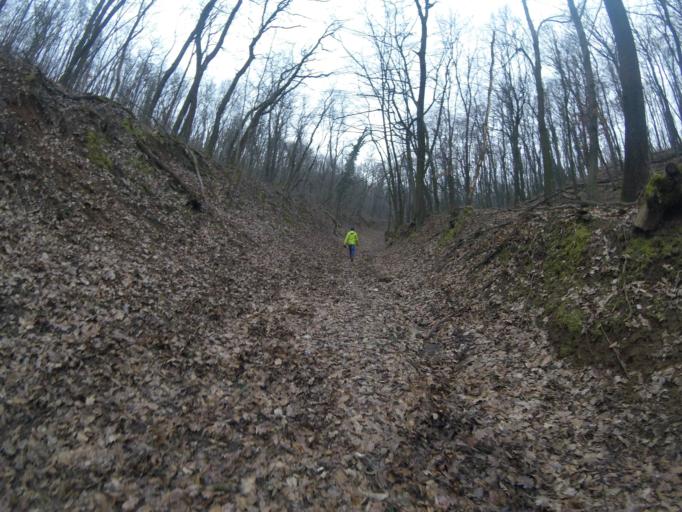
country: HU
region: Baranya
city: Mecseknadasd
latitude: 46.1401
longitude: 18.5205
